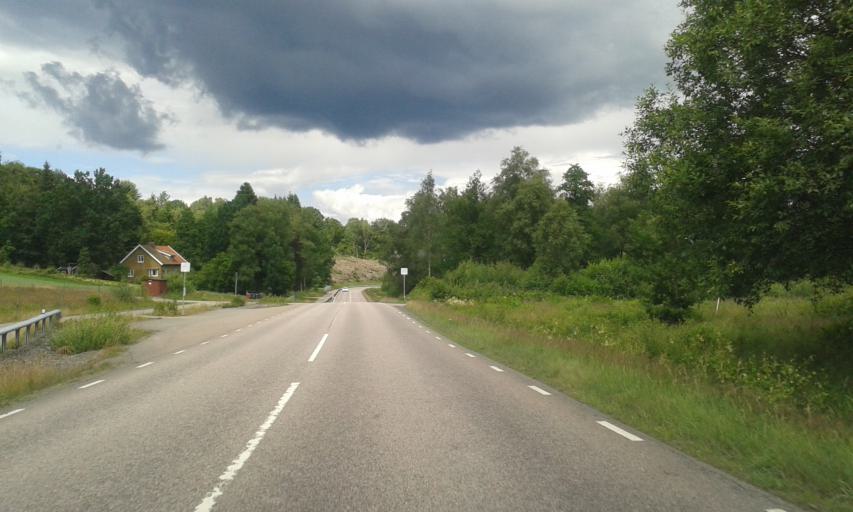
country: SE
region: Vaestra Goetaland
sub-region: Kungalvs Kommun
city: Diserod
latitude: 57.9031
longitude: 12.0087
